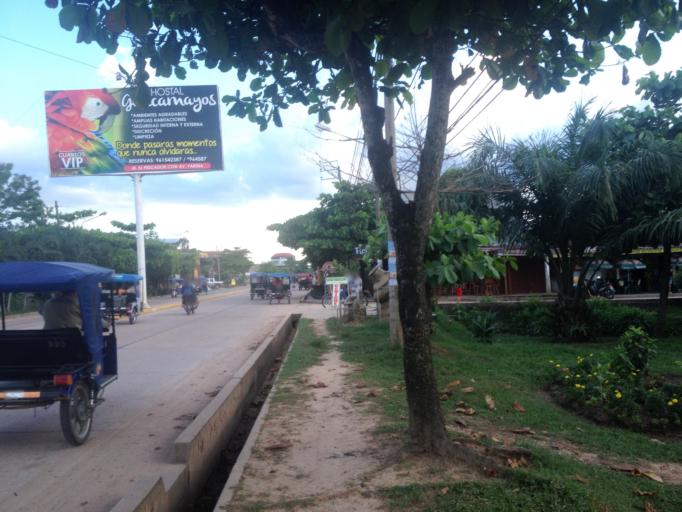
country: PE
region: Ucayali
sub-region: Provincia de Coronel Portillo
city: Pucallpa
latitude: -8.3760
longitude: -74.5686
